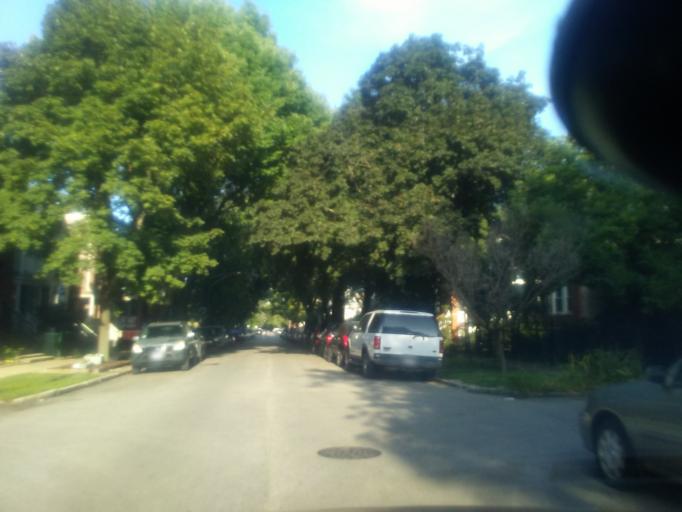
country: US
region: Illinois
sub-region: Cook County
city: Lincolnwood
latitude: 41.9789
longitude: -87.6716
